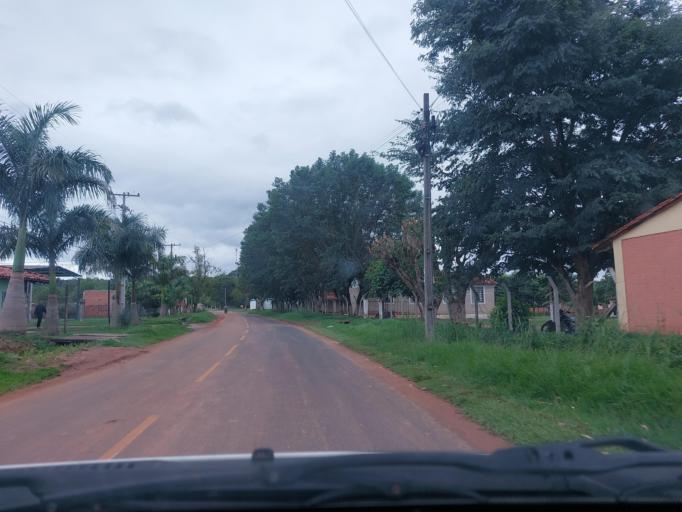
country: PY
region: San Pedro
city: Guayaybi
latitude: -24.6566
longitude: -56.4380
